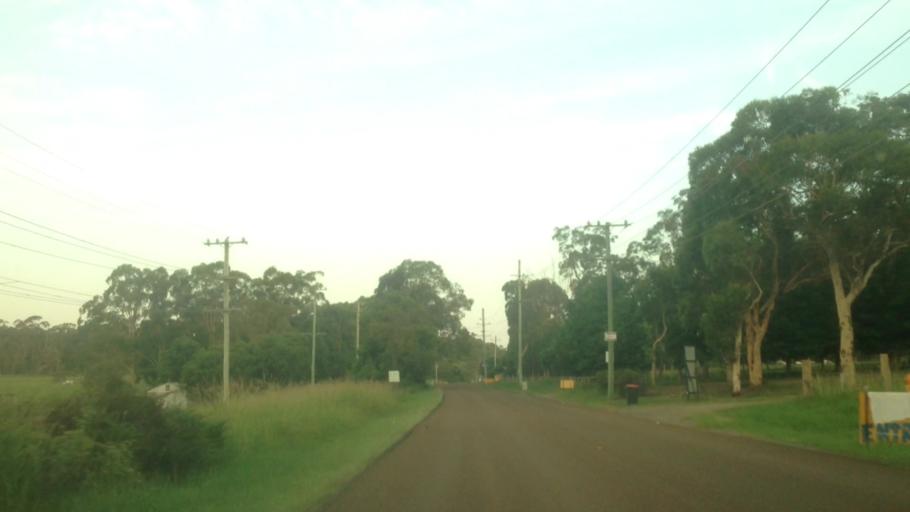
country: AU
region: New South Wales
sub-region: Lake Macquarie Shire
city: Dora Creek
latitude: -33.0735
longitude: 151.4807
